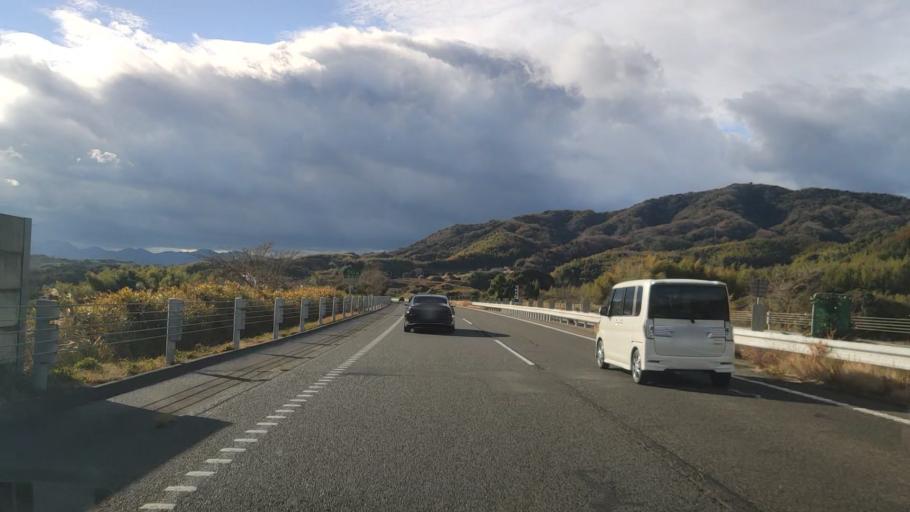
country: JP
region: Hyogo
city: Sumoto
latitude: 34.3945
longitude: 134.8597
